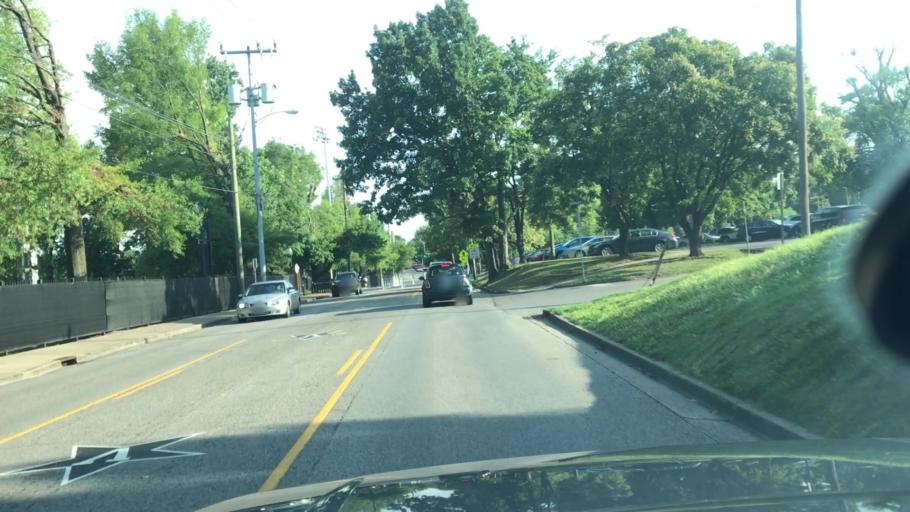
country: US
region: Tennessee
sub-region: Davidson County
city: Nashville
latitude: 36.1421
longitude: -86.8103
